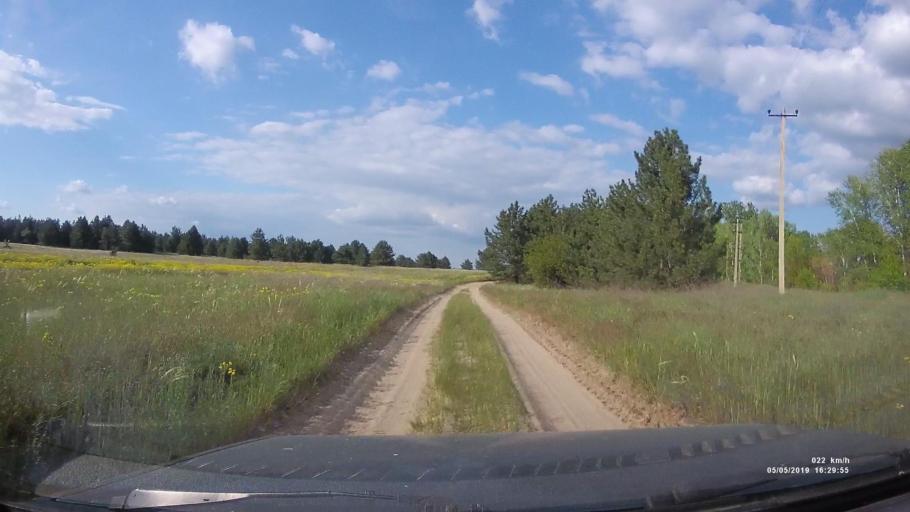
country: RU
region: Rostov
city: Ust'-Donetskiy
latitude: 47.7720
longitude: 41.0149
